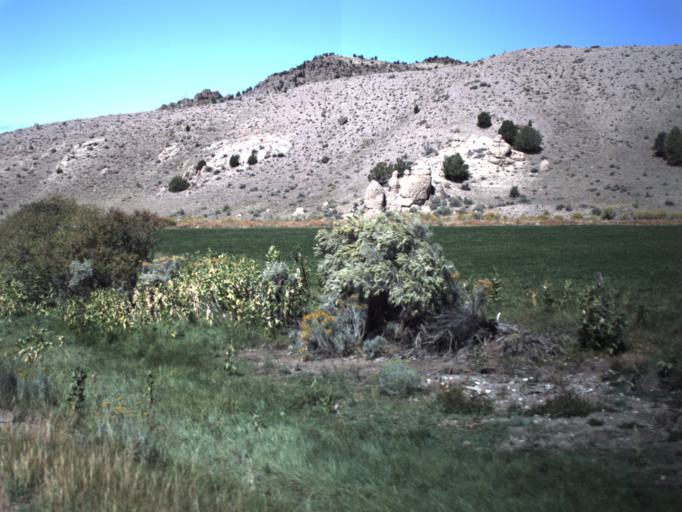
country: US
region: Utah
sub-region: Piute County
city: Junction
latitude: 38.1965
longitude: -112.1477
